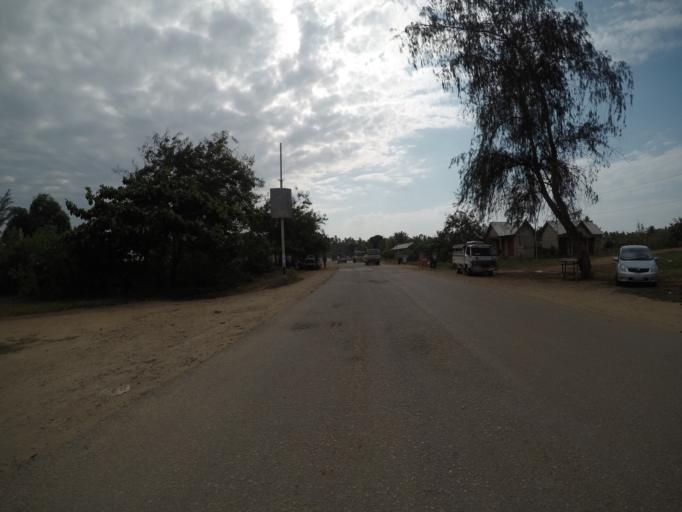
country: TZ
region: Zanzibar Central/South
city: Koani
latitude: -6.1954
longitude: 39.3040
